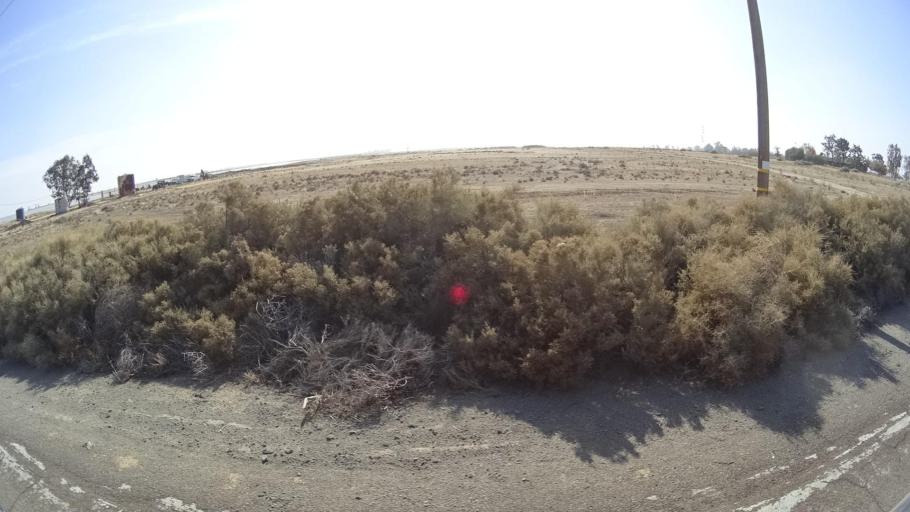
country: US
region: California
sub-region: Kern County
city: Oildale
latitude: 35.5299
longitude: -119.1008
